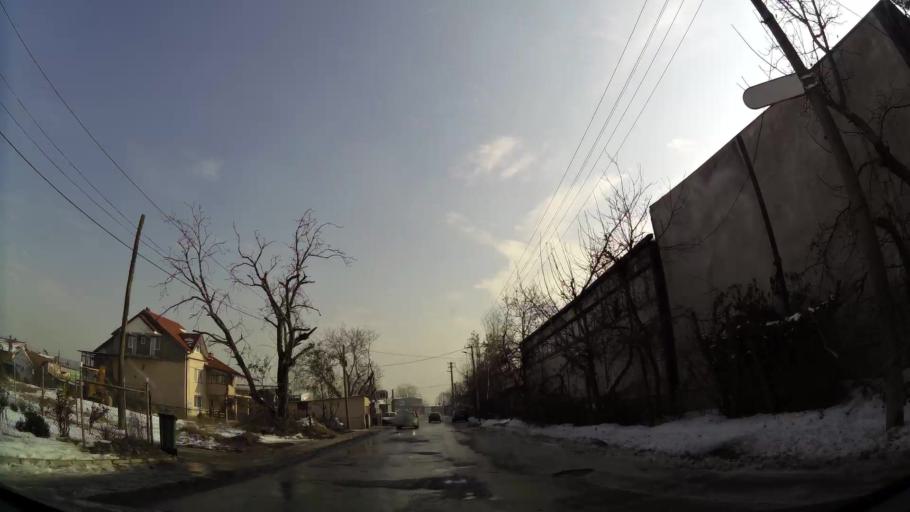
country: MK
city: Krushopek
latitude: 42.0147
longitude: 21.3811
